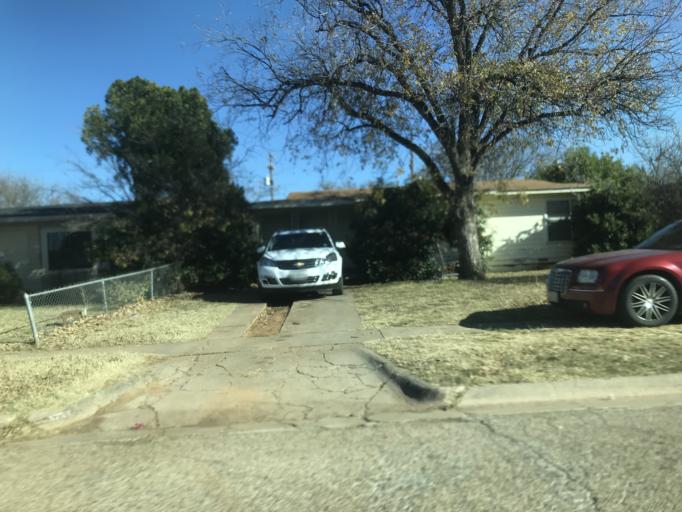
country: US
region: Texas
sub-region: Taylor County
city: Abilene
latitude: 32.4352
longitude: -99.7536
